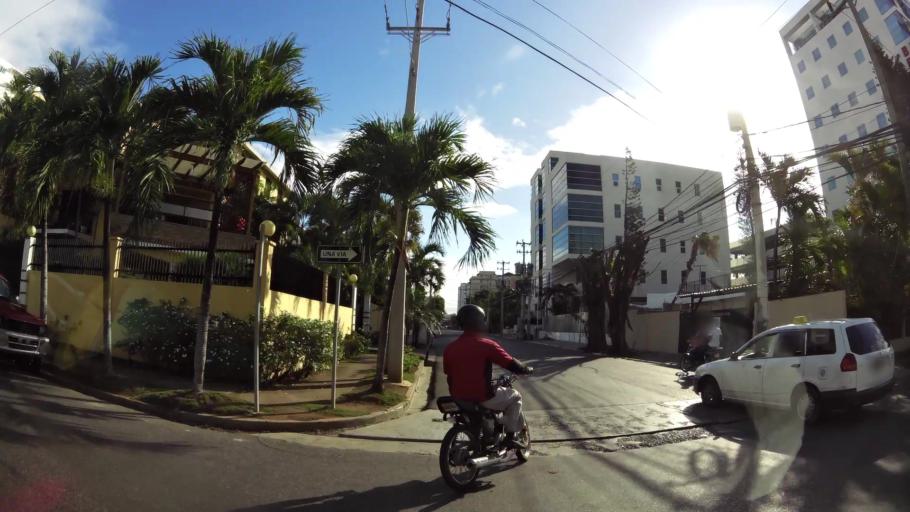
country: DO
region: Nacional
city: La Julia
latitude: 18.4708
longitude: -69.9381
